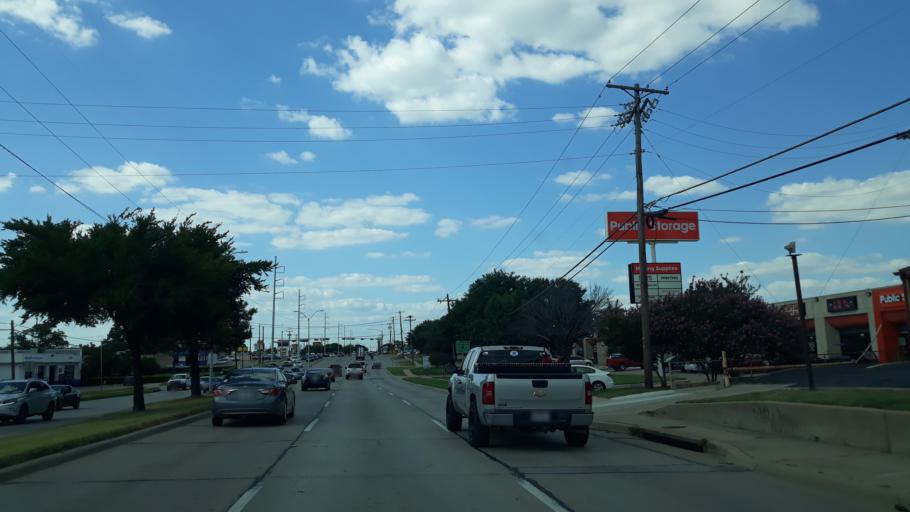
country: US
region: Texas
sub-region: Dallas County
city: Irving
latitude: 32.8263
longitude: -96.9937
